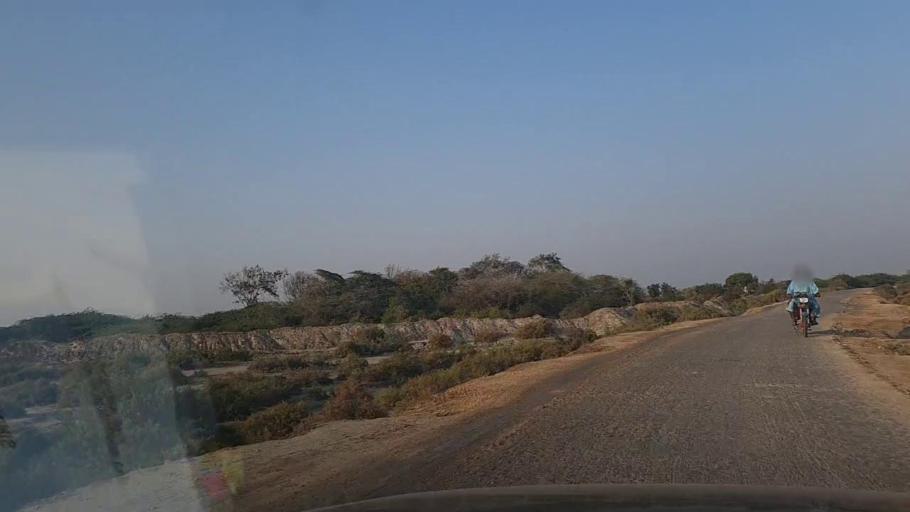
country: PK
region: Sindh
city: Keti Bandar
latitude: 24.2926
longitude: 67.5829
